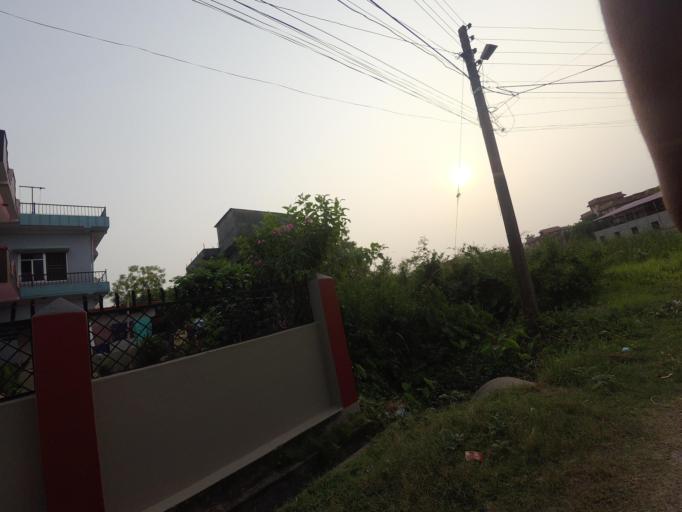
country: NP
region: Western Region
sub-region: Lumbini Zone
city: Bhairahawa
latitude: 27.5168
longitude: 83.4480
